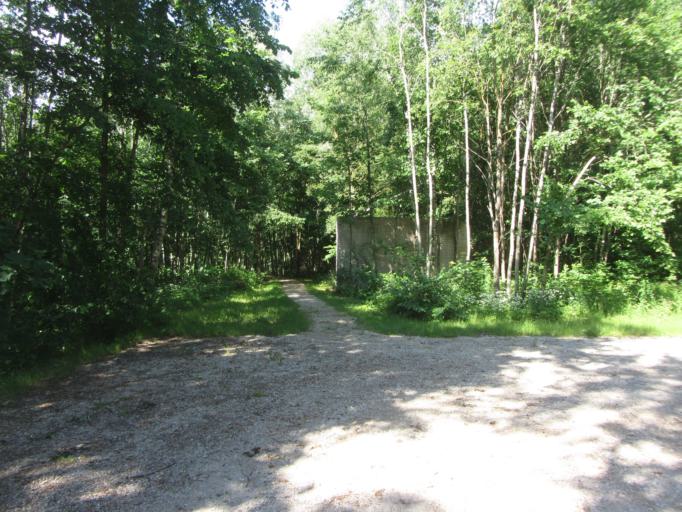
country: LT
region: Panevezys
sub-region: Birzai
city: Birzai
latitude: 56.3845
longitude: 24.7010
